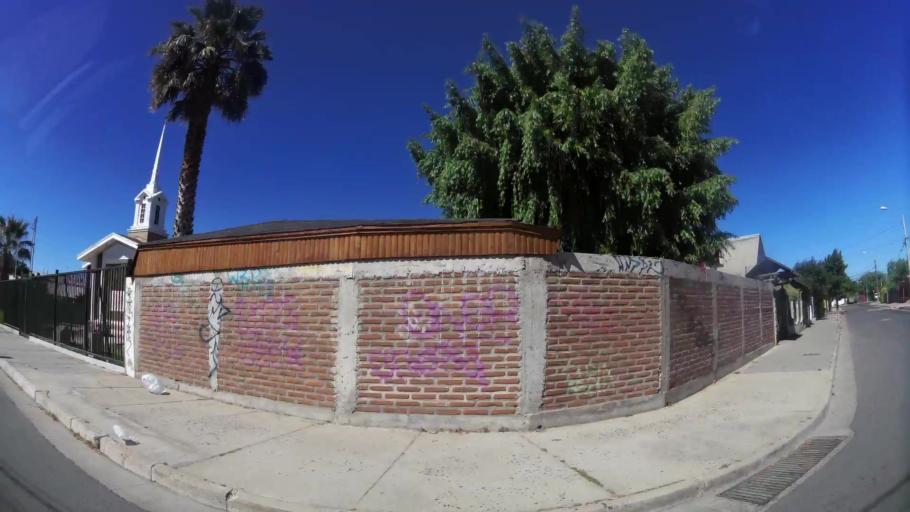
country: CL
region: Valparaiso
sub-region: Provincia de Marga Marga
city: Quilpue
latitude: -33.3144
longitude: -71.4080
